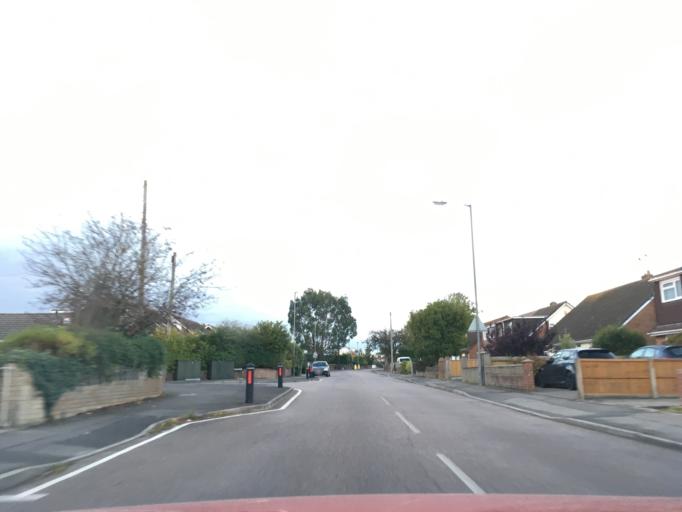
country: GB
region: England
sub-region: South Gloucestershire
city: Almondsbury
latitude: 51.5333
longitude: -2.5620
